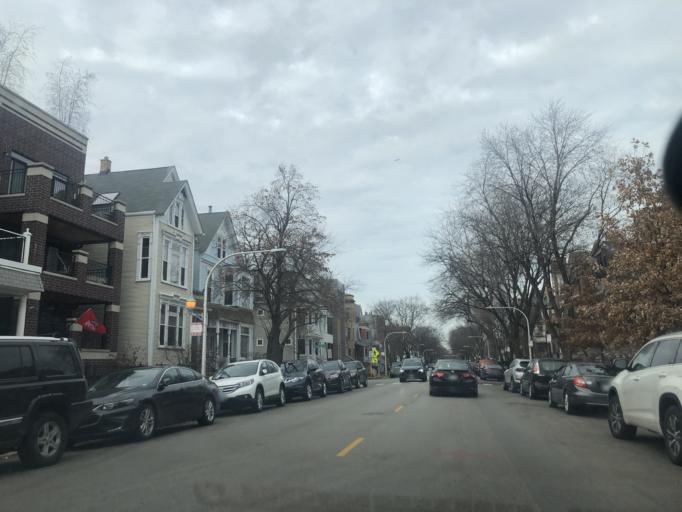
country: US
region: Illinois
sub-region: Cook County
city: Chicago
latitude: 41.9402
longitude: -87.6589
